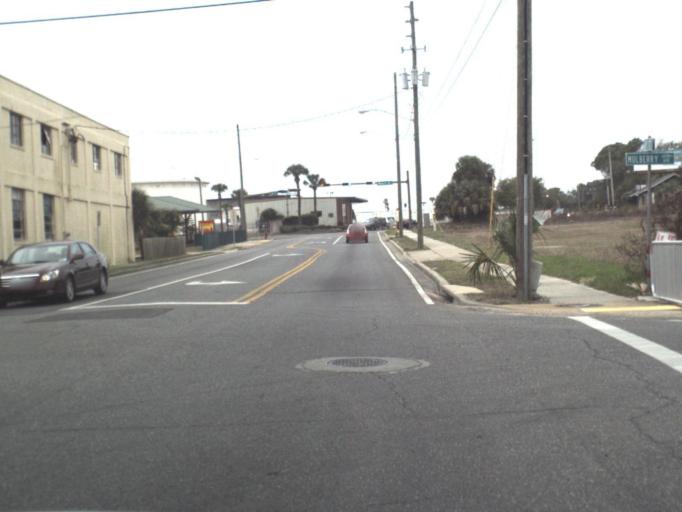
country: US
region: Florida
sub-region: Bay County
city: Panama City
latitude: 30.1589
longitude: -85.6650
